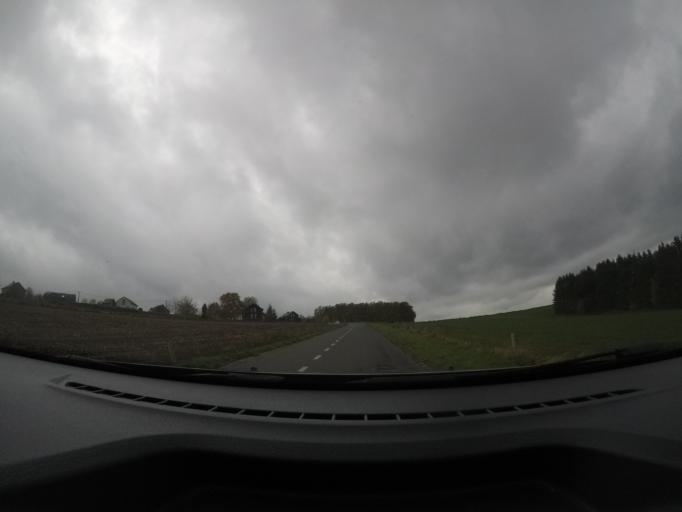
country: BE
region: Wallonia
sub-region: Province du Luxembourg
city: Bertogne
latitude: 50.1253
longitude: 5.7174
